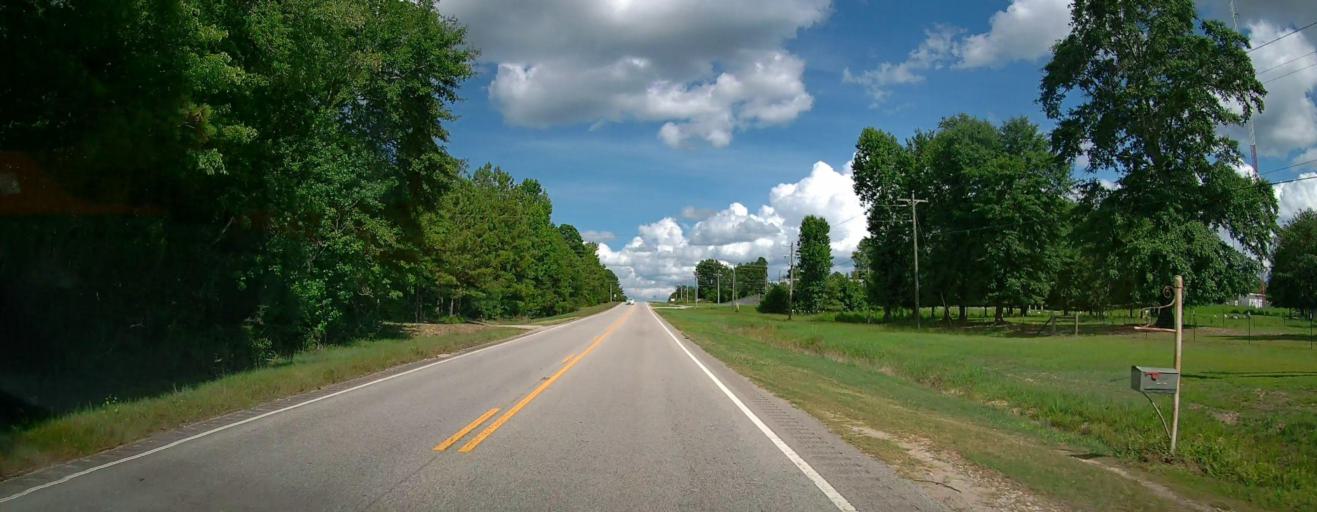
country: US
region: Alabama
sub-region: Macon County
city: Tuskegee
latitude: 32.4645
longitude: -85.5659
